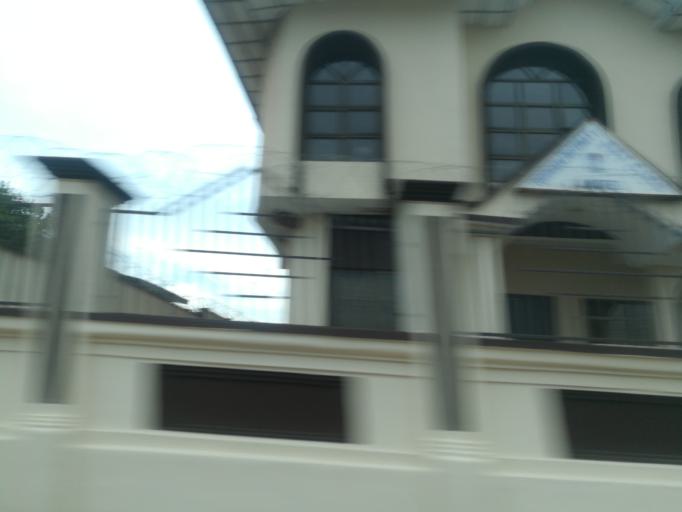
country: NG
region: Oyo
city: Moniya
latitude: 7.4546
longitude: 3.9112
